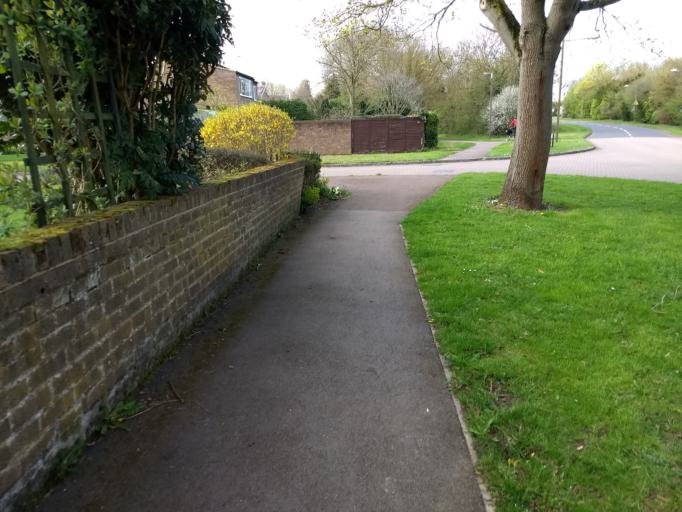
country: GB
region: England
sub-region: Milton Keynes
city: Simpson
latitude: 52.0242
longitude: -0.7206
